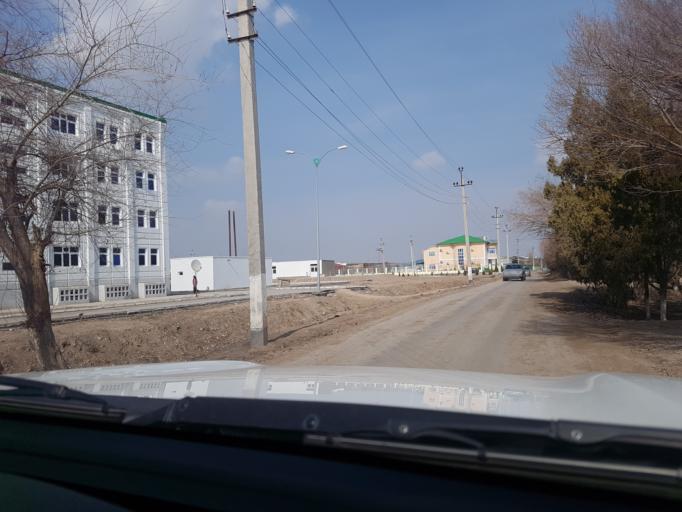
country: TM
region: Dasoguz
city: Dasoguz
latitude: 41.8398
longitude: 59.9214
